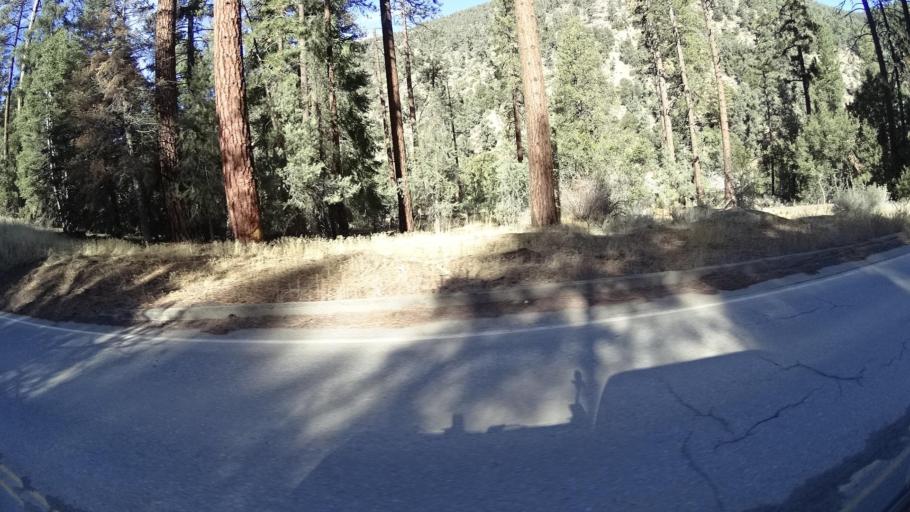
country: US
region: California
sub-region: Kern County
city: Pine Mountain Club
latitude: 34.8478
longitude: -119.0939
